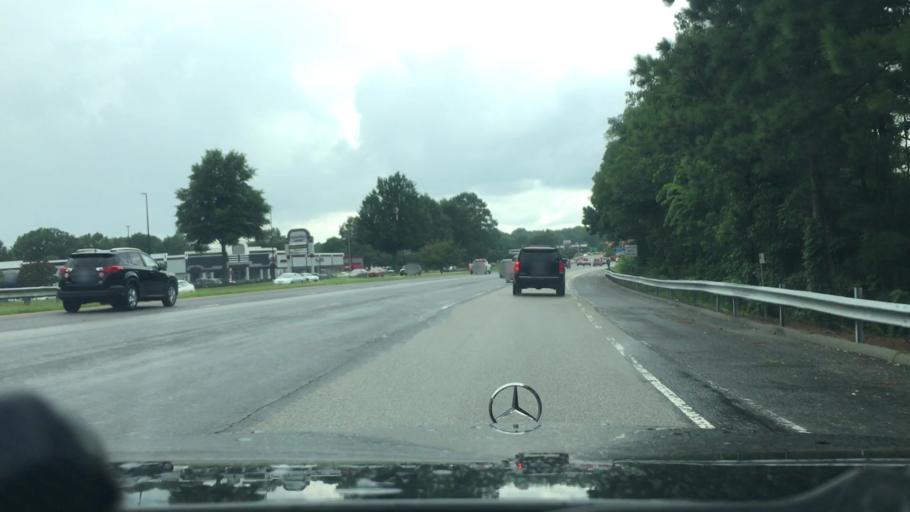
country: US
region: Virginia
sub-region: Chesterfield County
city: Bon Air
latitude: 37.4961
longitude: -77.5639
